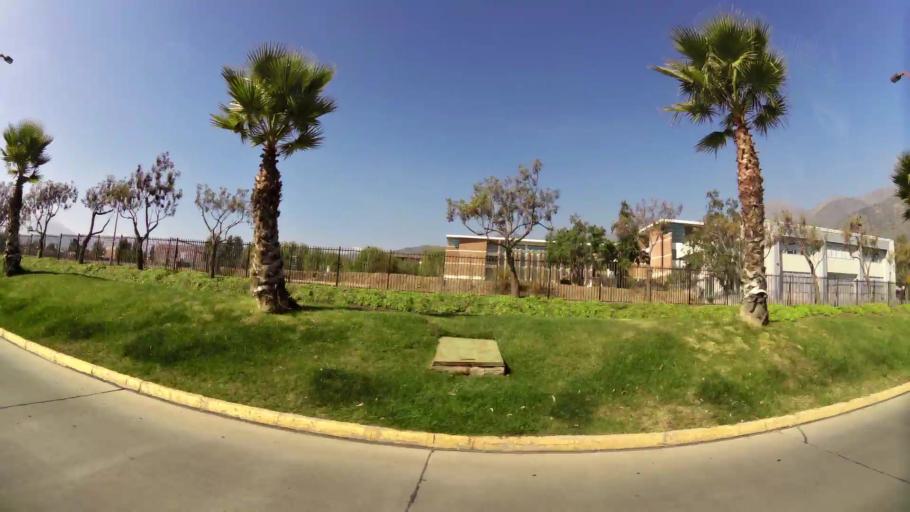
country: CL
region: Santiago Metropolitan
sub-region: Provincia de Santiago
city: Villa Presidente Frei, Nunoa, Santiago, Chile
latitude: -33.4028
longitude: -70.5092
